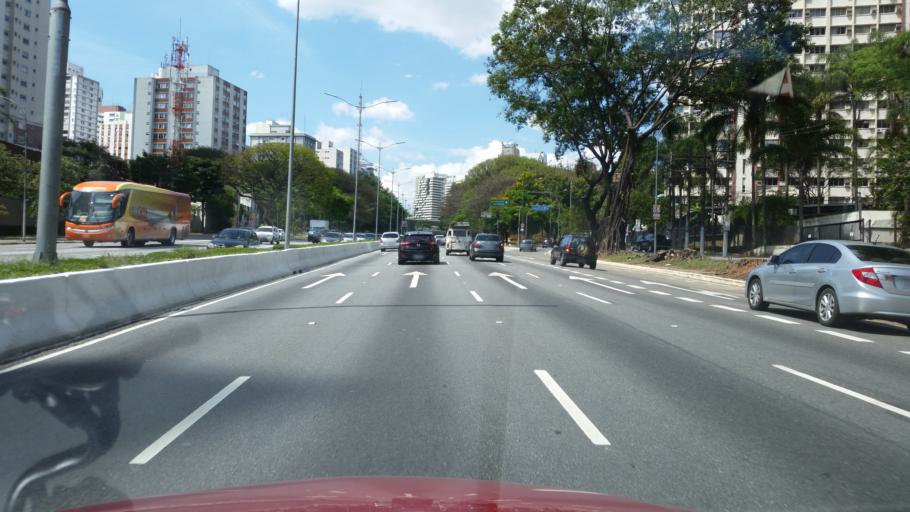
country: BR
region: Sao Paulo
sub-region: Sao Paulo
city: Sao Paulo
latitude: -23.5791
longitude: -46.6468
